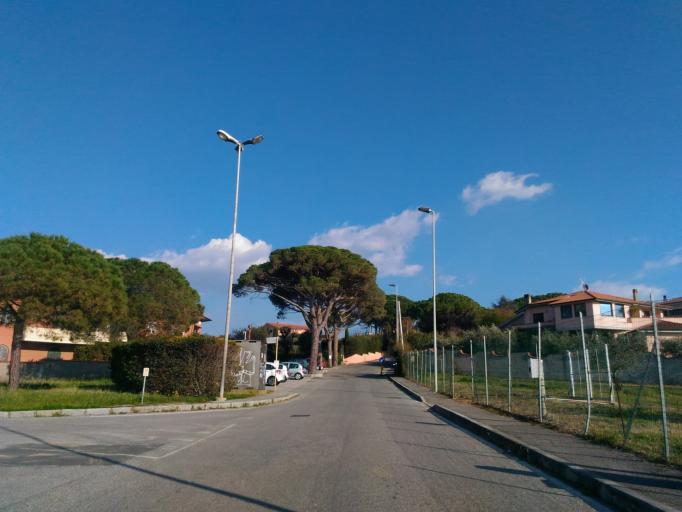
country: IT
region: Tuscany
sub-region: Provincia di Livorno
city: Livorno
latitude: 43.5108
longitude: 10.3383
